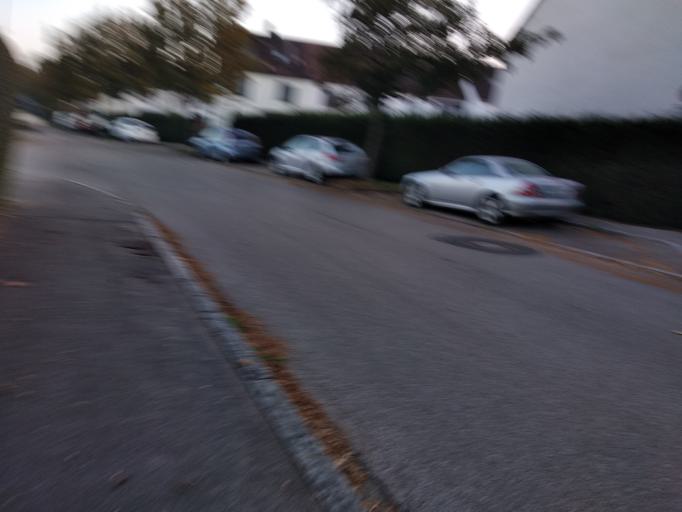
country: DE
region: Bavaria
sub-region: Upper Bavaria
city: Kirchheim bei Muenchen
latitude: 48.1632
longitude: 11.7639
